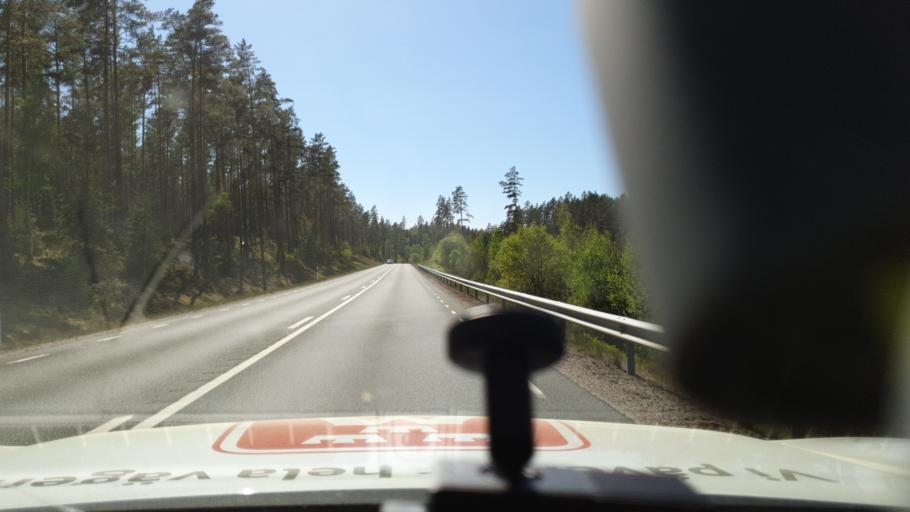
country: SE
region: Kalmar
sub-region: Hultsfreds Kommun
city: Virserum
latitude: 57.3975
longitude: 15.3855
